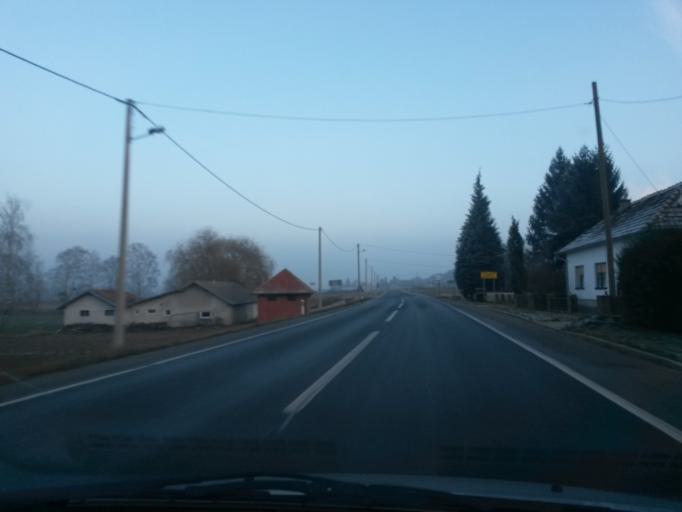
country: HR
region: Varazdinska
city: Ludbreg
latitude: 46.2348
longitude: 16.6496
